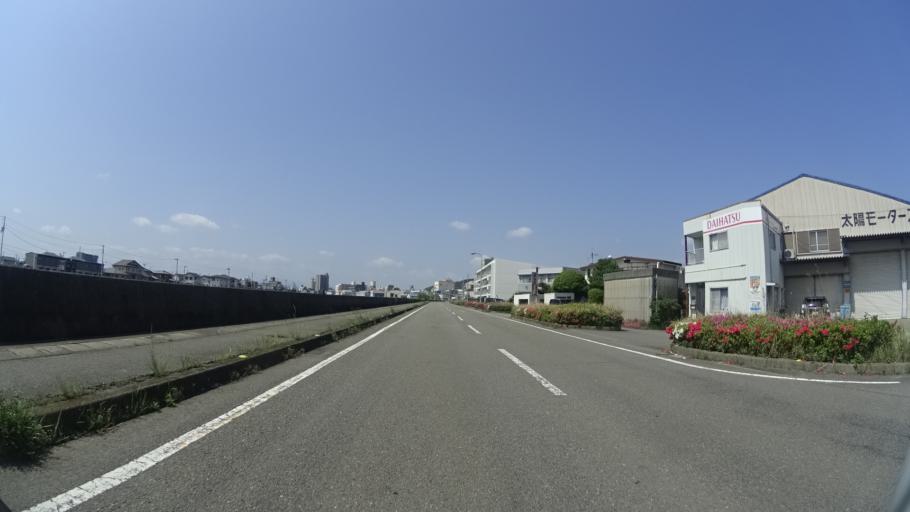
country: JP
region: Tokushima
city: Narutocho-mitsuishi
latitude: 34.1844
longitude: 134.6152
